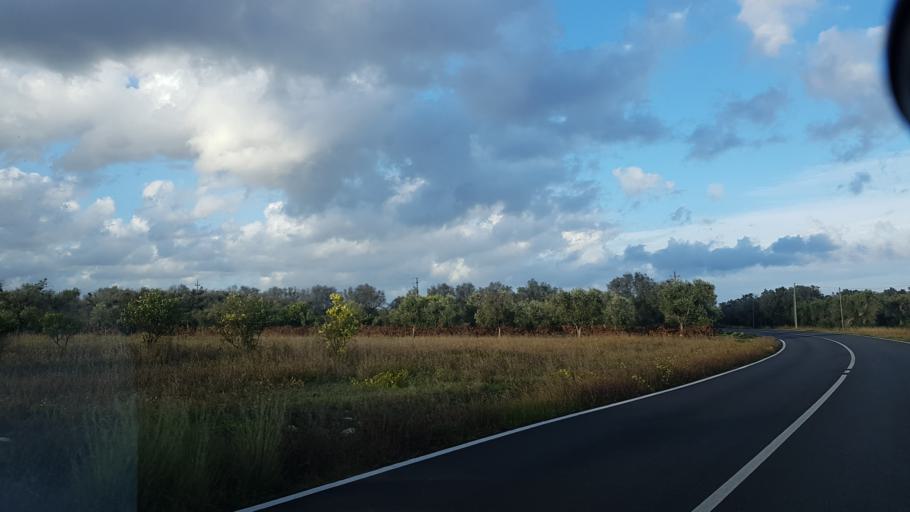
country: IT
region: Apulia
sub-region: Provincia di Brindisi
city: San Pietro Vernotico
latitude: 40.5045
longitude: 18.0074
